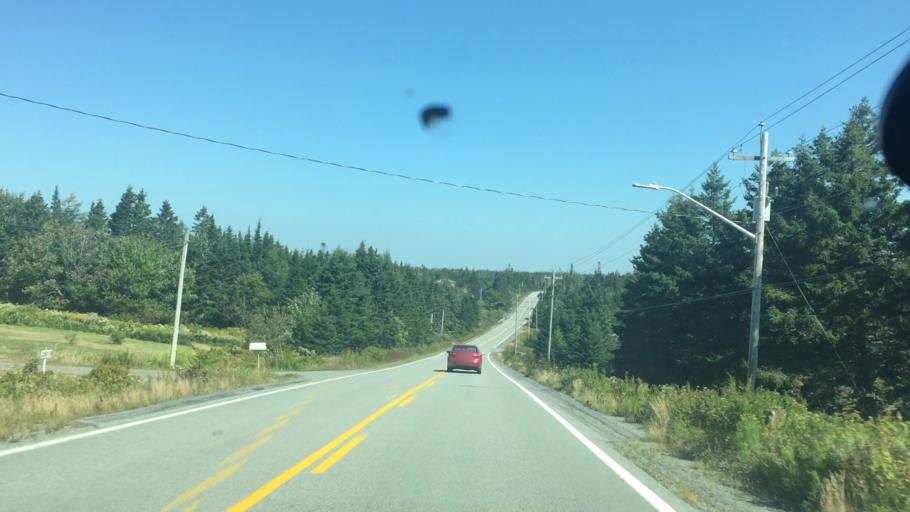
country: CA
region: Nova Scotia
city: Antigonish
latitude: 44.9405
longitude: -62.2672
